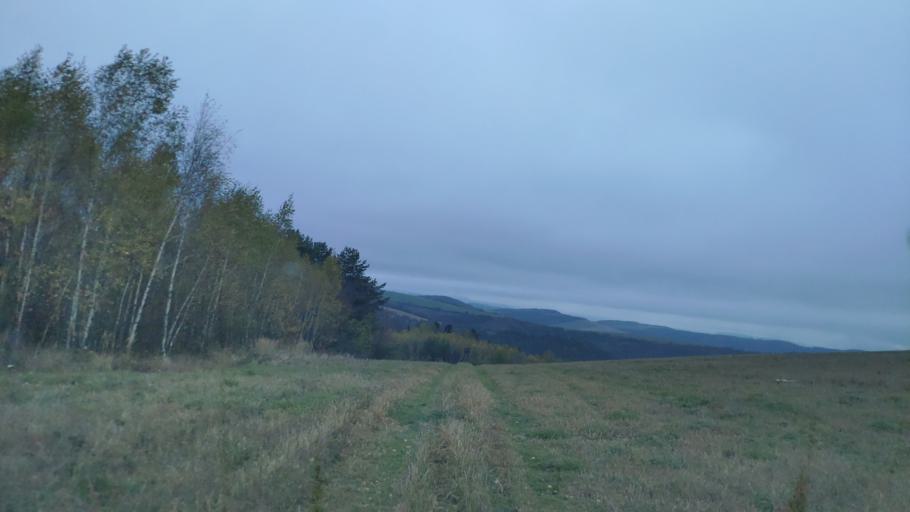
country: SK
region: Presovsky
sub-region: Okres Presov
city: Presov
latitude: 48.9325
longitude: 21.0867
